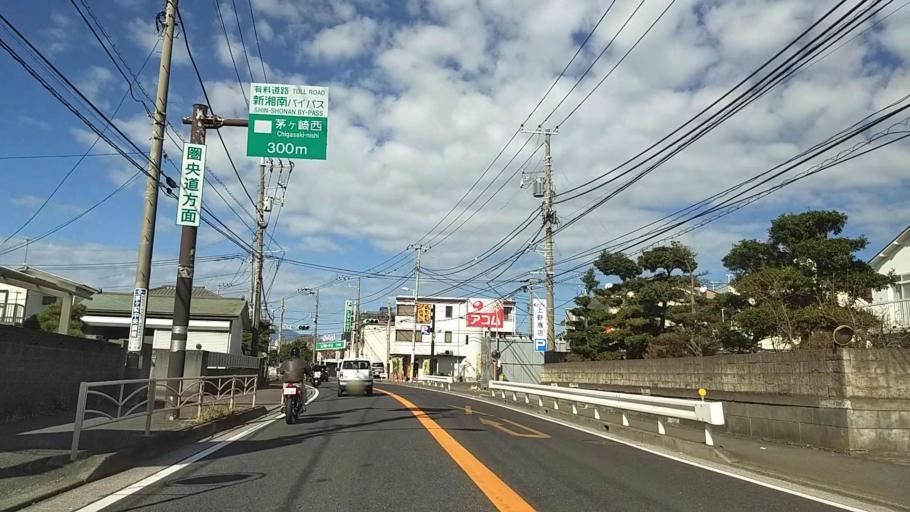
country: JP
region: Kanagawa
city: Chigasaki
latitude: 35.3319
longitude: 139.3880
